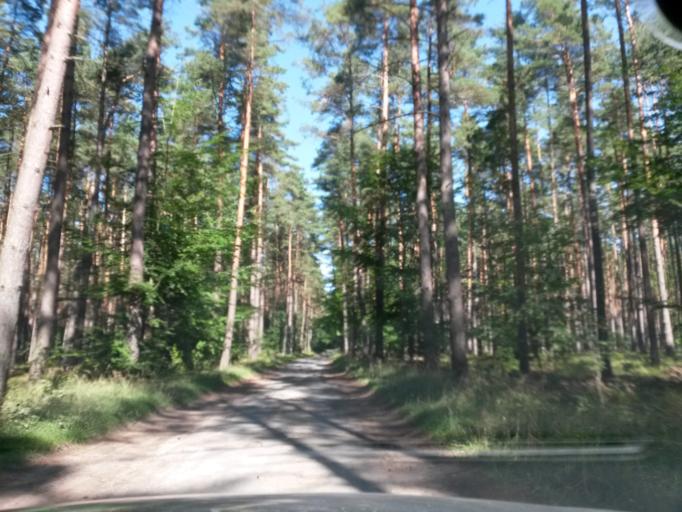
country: DE
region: Brandenburg
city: Templin
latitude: 53.2066
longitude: 13.4539
